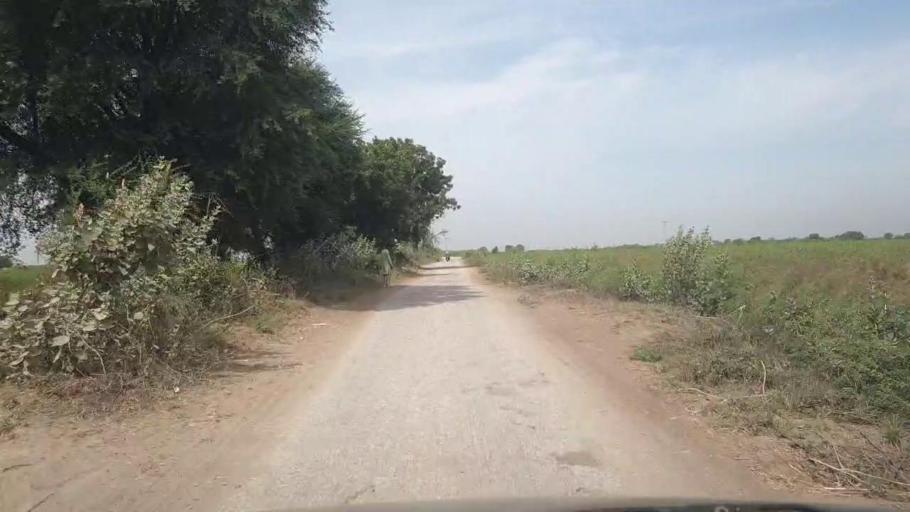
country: PK
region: Sindh
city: Kunri
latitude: 25.2270
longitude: 69.6763
